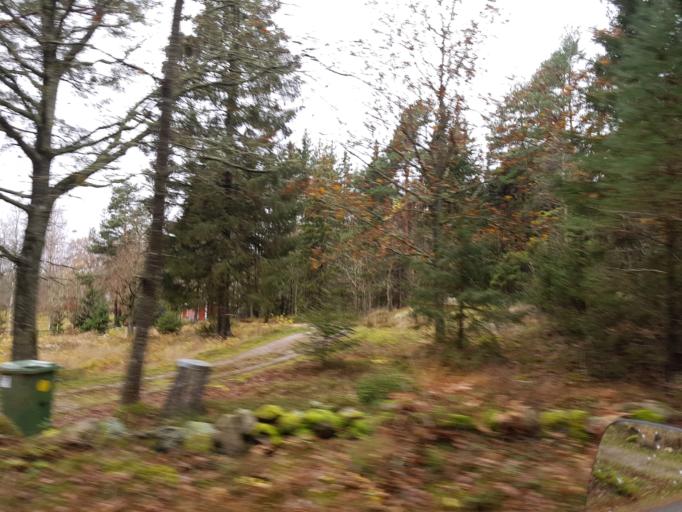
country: SE
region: Vaestra Goetaland
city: Svanesund
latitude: 58.1761
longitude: 11.7693
